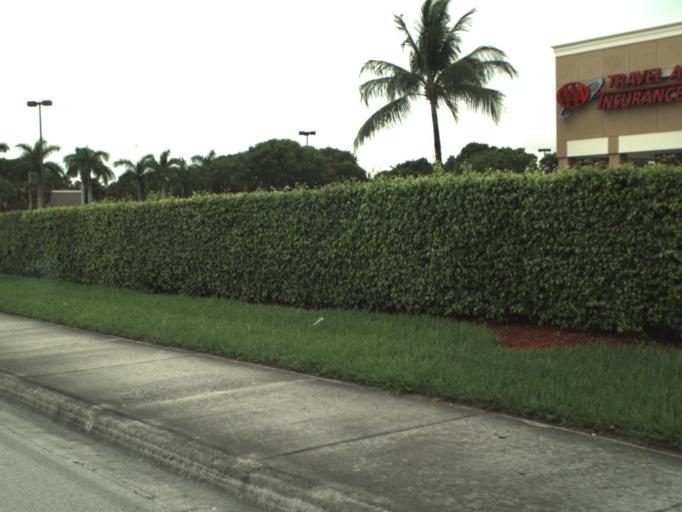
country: US
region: Florida
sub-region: Palm Beach County
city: Kings Point
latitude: 26.4609
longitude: -80.1227
